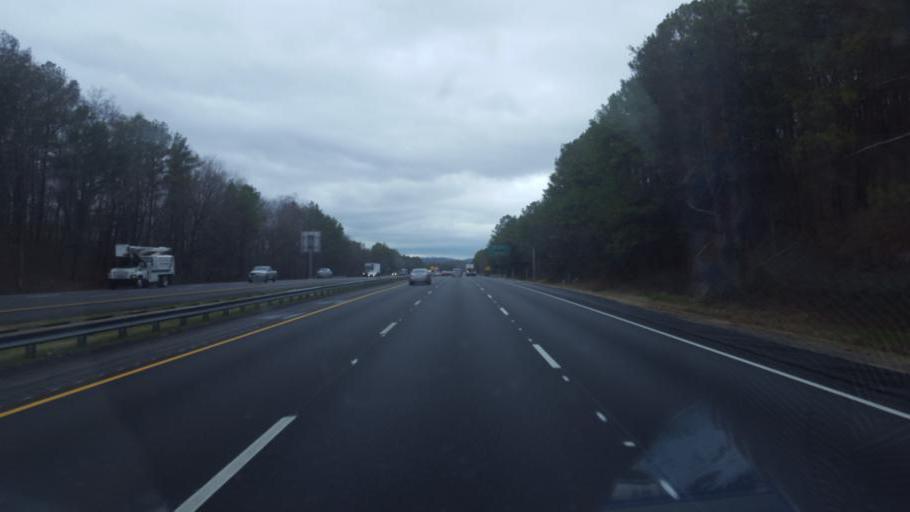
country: US
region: Georgia
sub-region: Whitfield County
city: Varnell
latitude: 34.8725
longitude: -85.0406
